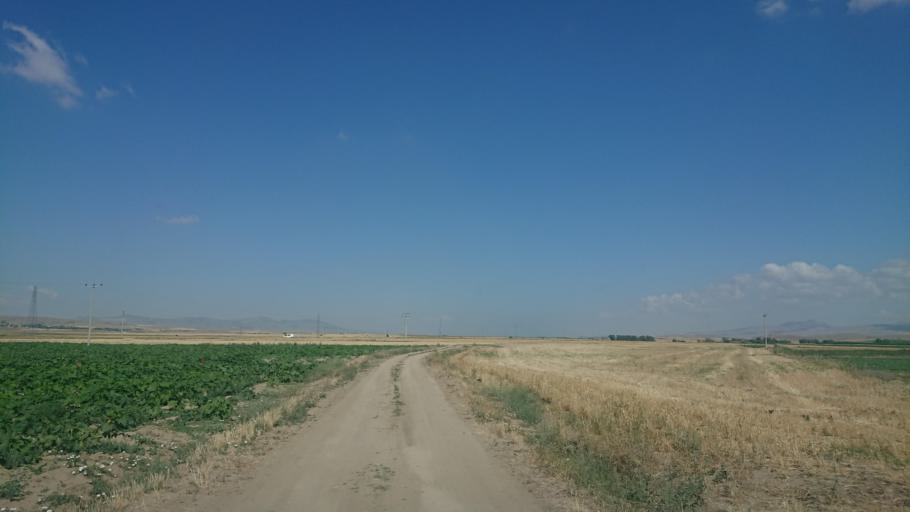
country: TR
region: Aksaray
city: Sariyahsi
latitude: 38.9851
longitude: 33.9053
